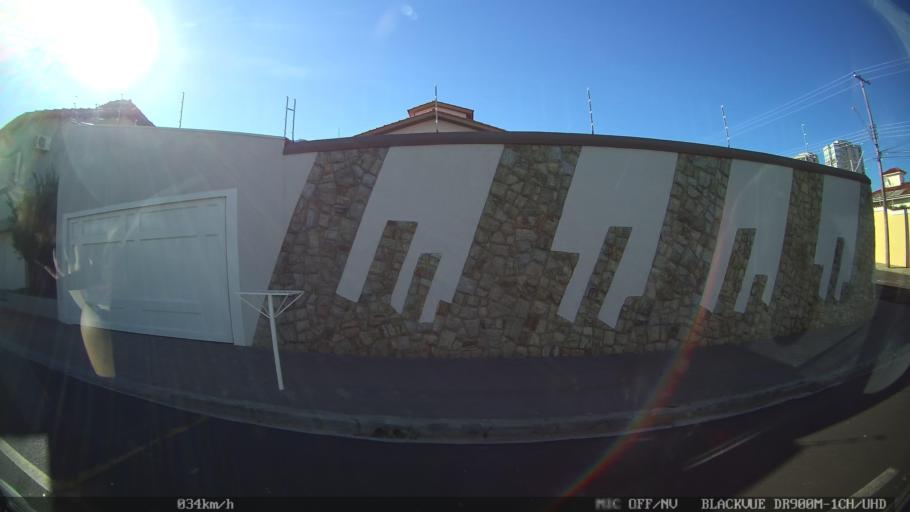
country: BR
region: Sao Paulo
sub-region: Franca
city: Franca
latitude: -20.5447
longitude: -47.4063
